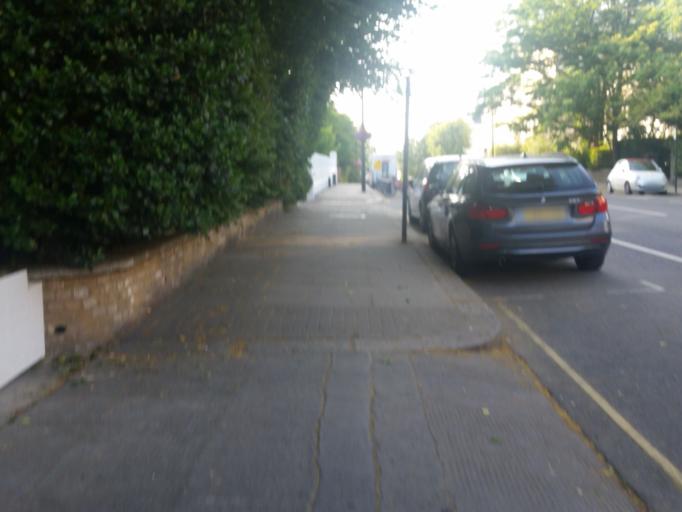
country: GB
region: England
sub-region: Greater London
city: Kensington
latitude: 51.5114
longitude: -0.2057
